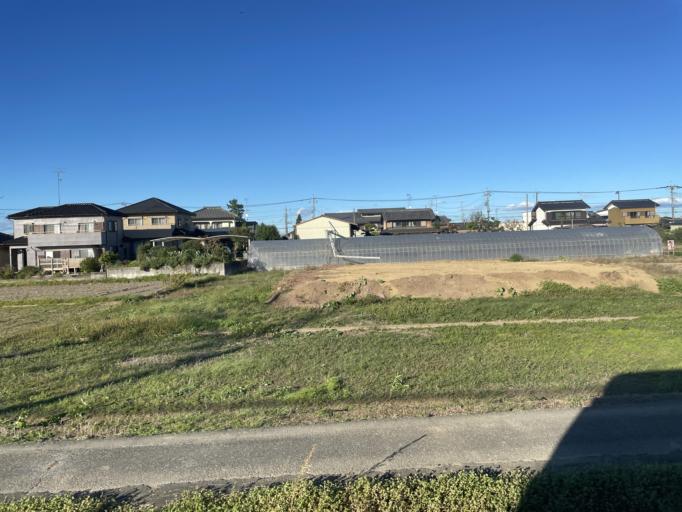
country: JP
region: Tochigi
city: Fujioka
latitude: 36.2026
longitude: 139.6671
